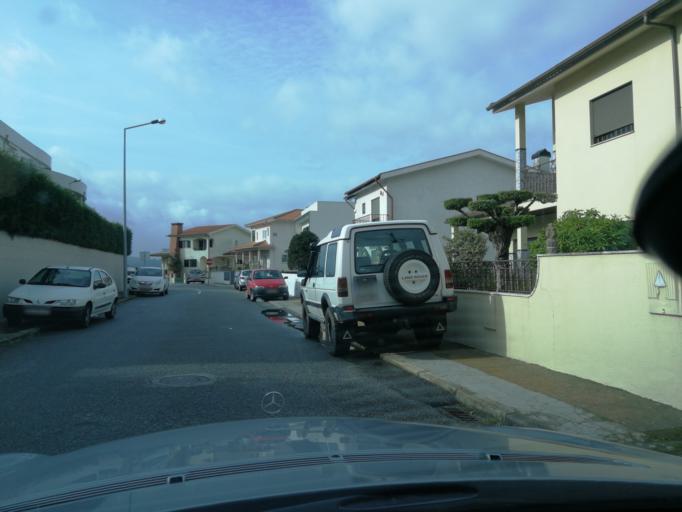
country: PT
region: Braga
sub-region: Braga
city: Braga
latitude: 41.5294
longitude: -8.4156
